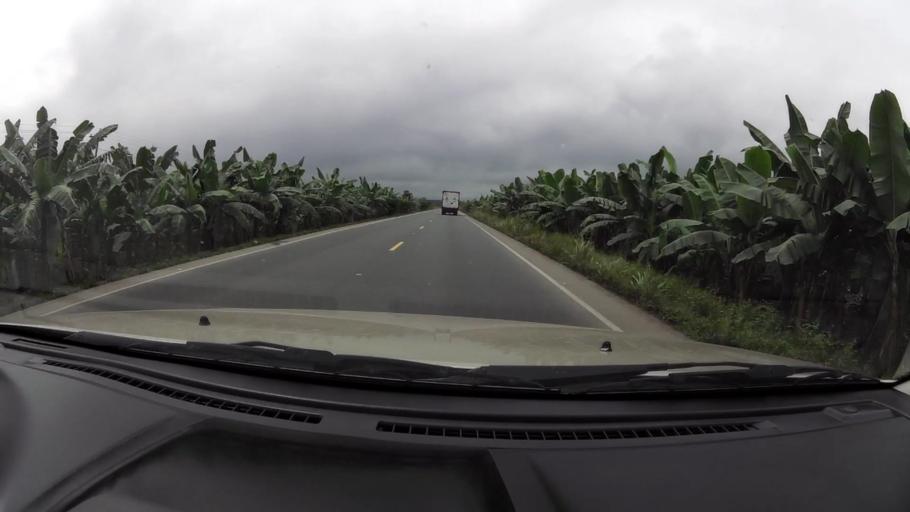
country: EC
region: Guayas
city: Balao
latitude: -2.9193
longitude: -79.7075
